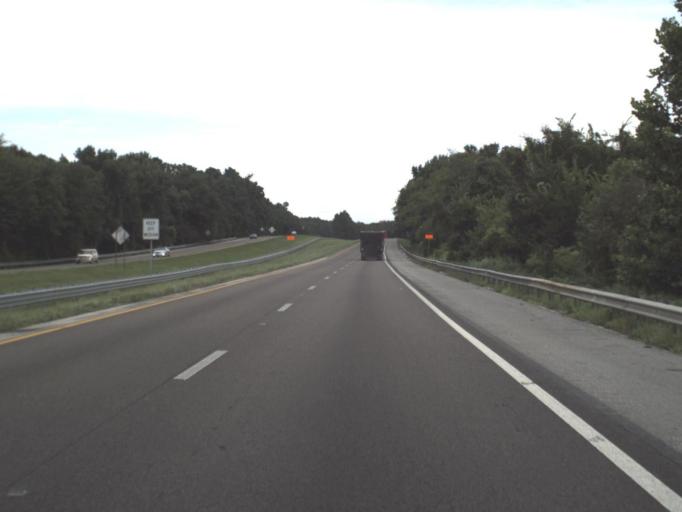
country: US
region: Florida
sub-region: Hernando County
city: Hill 'n Dale
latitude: 28.4355
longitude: -82.2809
